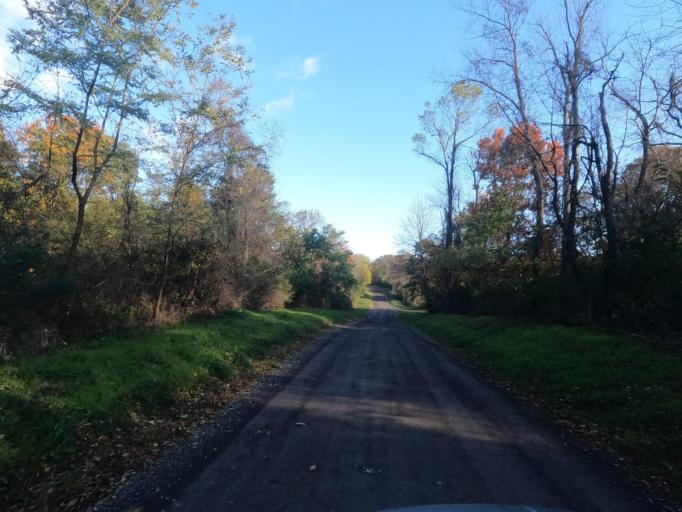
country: US
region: West Virginia
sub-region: Morgan County
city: Berkeley Springs
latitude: 39.6123
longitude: -78.4919
